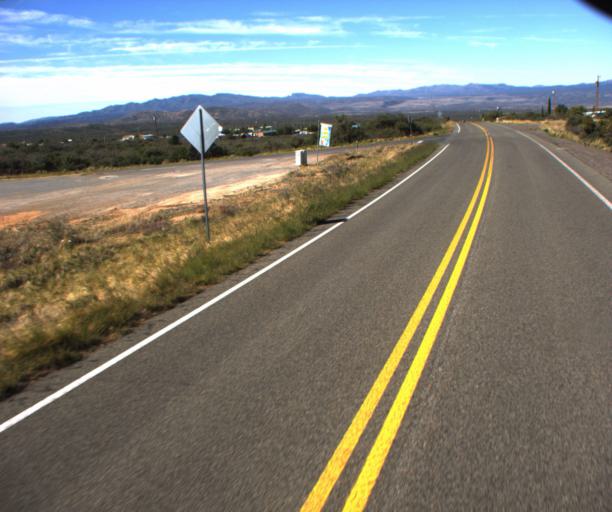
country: US
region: Arizona
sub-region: Yavapai County
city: Prescott
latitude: 34.4243
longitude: -112.5892
